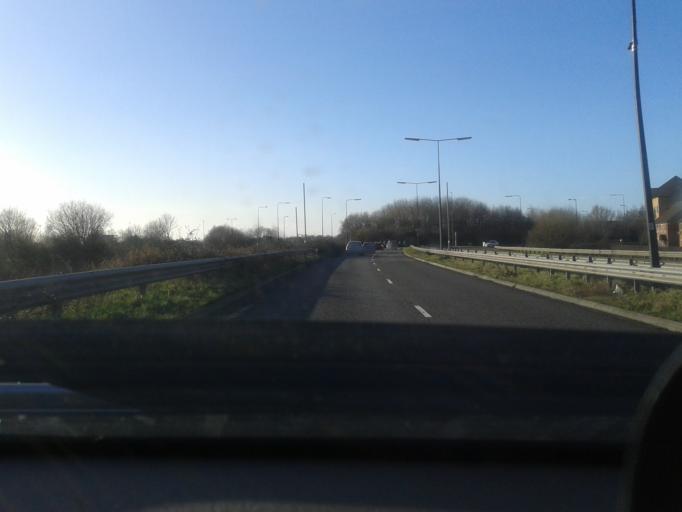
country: GB
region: England
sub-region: North Somerset
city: Hutton
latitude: 51.3450
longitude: -2.9284
